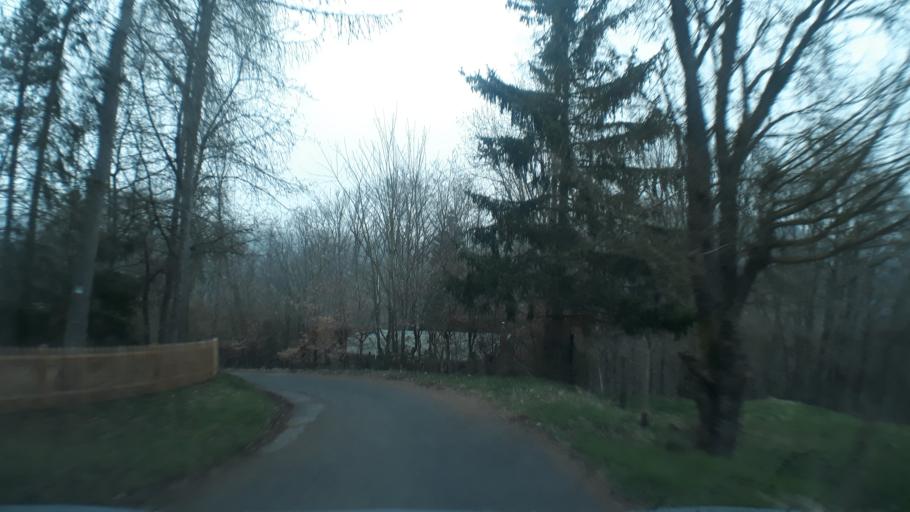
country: DE
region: North Rhine-Westphalia
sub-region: Regierungsbezirk Koln
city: Nettersheim
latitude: 50.5103
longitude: 6.5844
